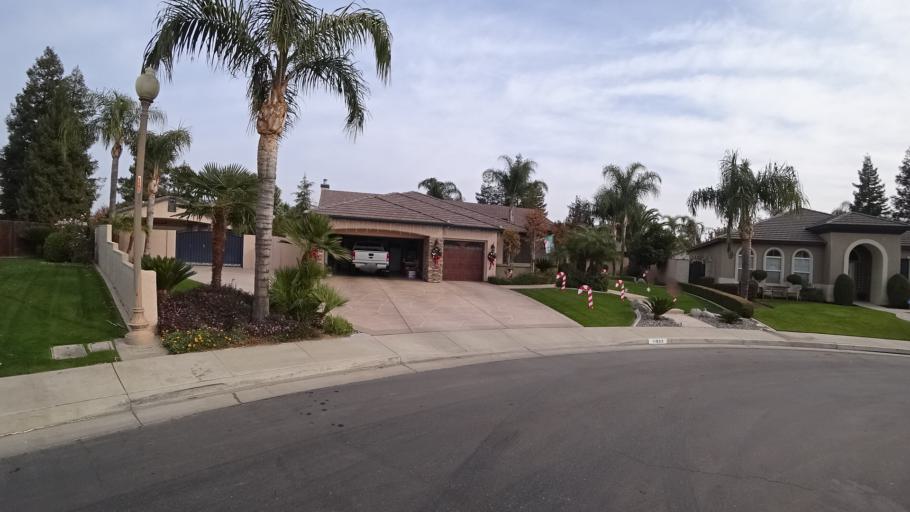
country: US
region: California
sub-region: Kern County
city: Rosedale
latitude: 35.3470
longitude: -119.1352
